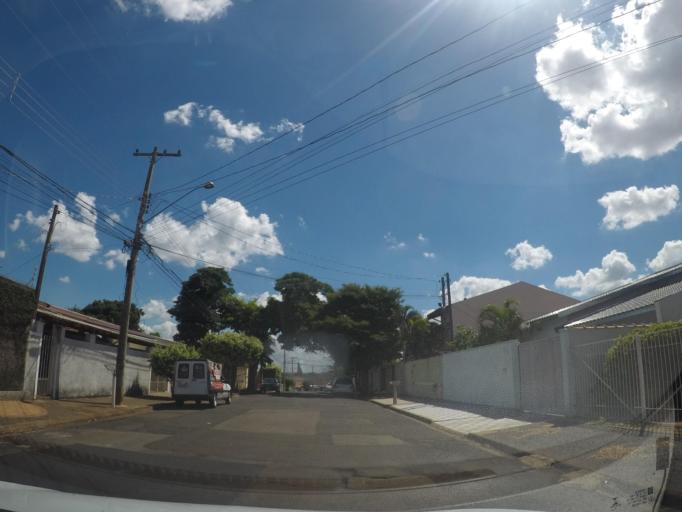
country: BR
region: Sao Paulo
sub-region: Sumare
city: Sumare
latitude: -22.8338
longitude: -47.2692
